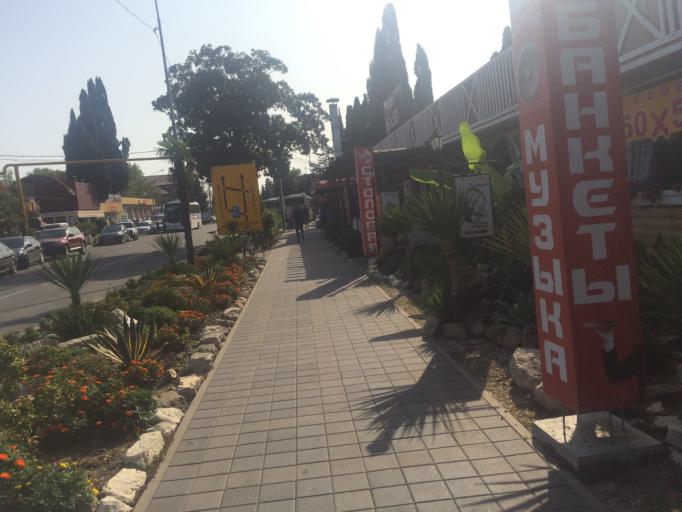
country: RU
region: Krasnodarskiy
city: Adler
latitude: 43.3916
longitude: 39.9861
